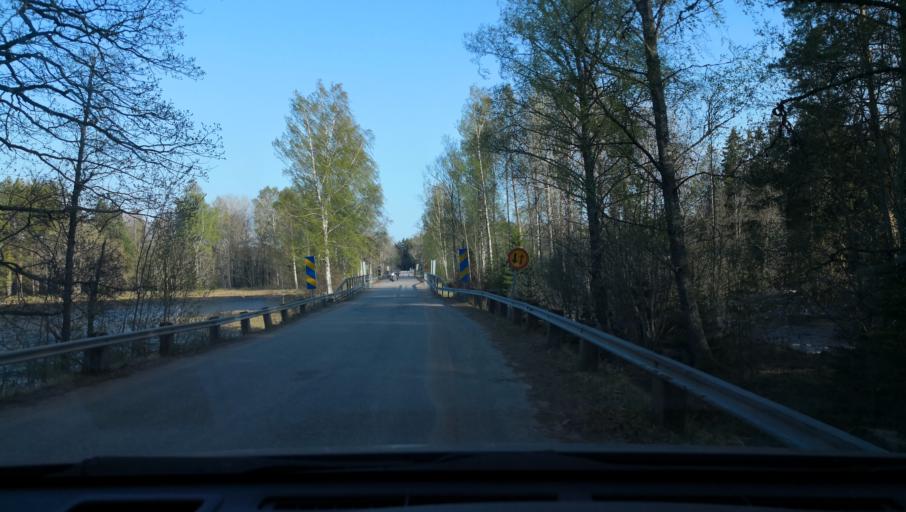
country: SE
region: Uppsala
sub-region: Heby Kommun
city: Tarnsjo
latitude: 60.2690
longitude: 16.9106
